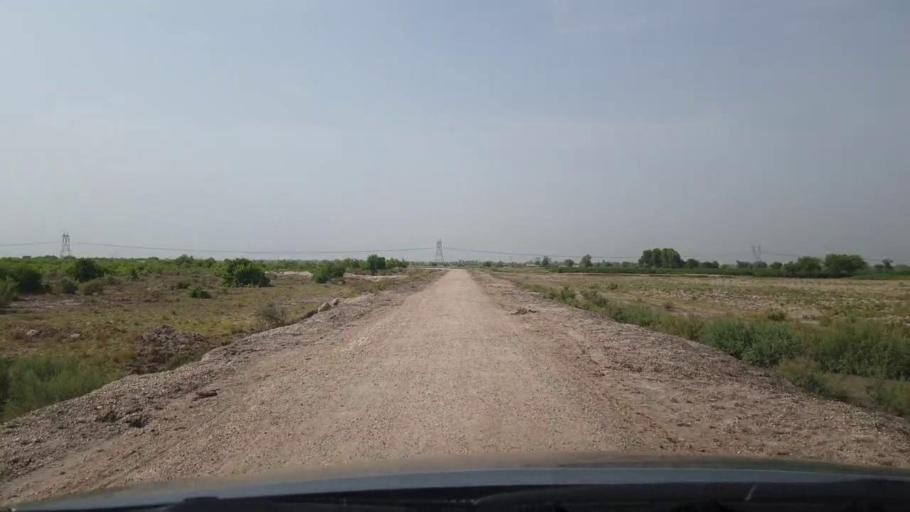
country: PK
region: Sindh
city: Rohri
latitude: 27.6809
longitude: 69.0122
